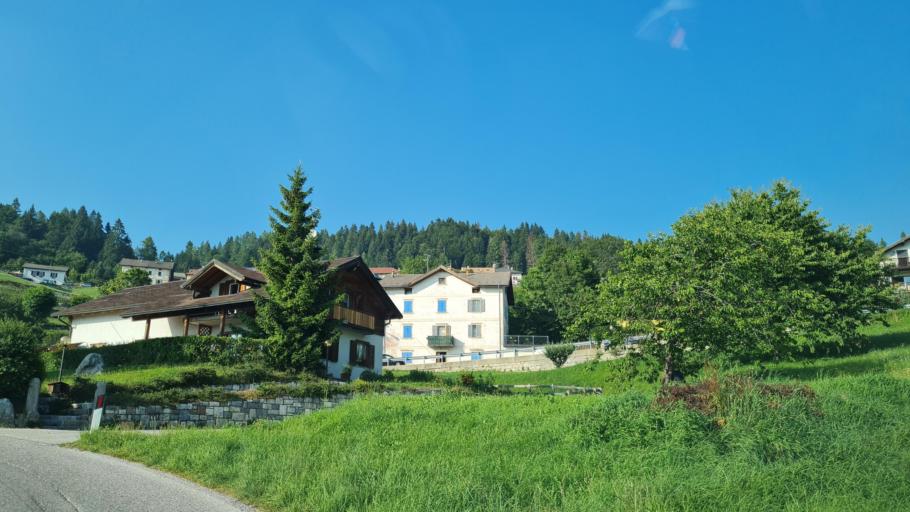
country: IT
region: Trentino-Alto Adige
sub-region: Provincia di Trento
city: Gionghi-Cappella
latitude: 45.9407
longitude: 11.2792
